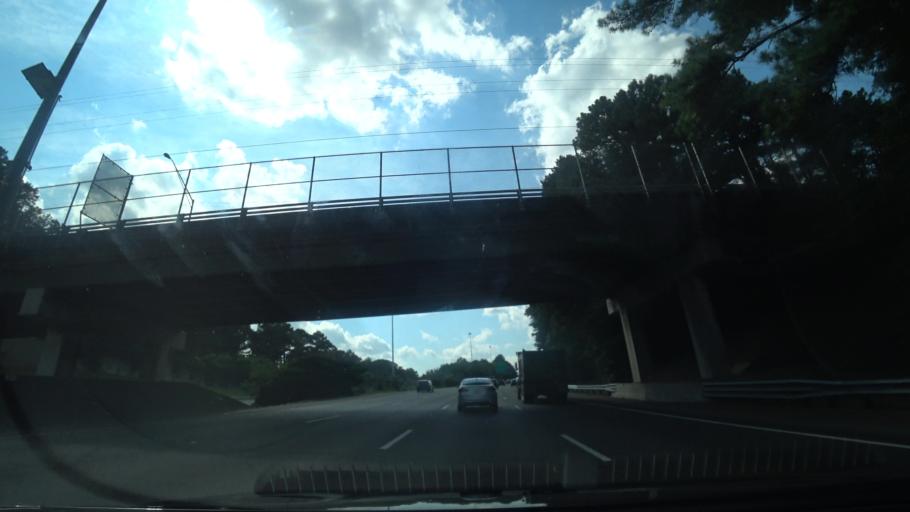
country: US
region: Georgia
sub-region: Fulton County
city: East Point
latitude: 33.7599
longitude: -84.4824
